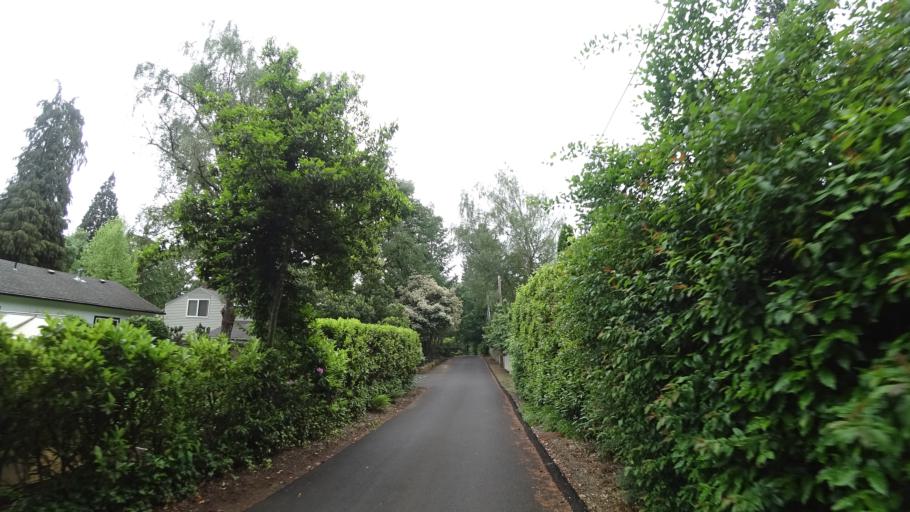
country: US
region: Oregon
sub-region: Clackamas County
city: Milwaukie
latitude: 45.4505
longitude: -122.6488
